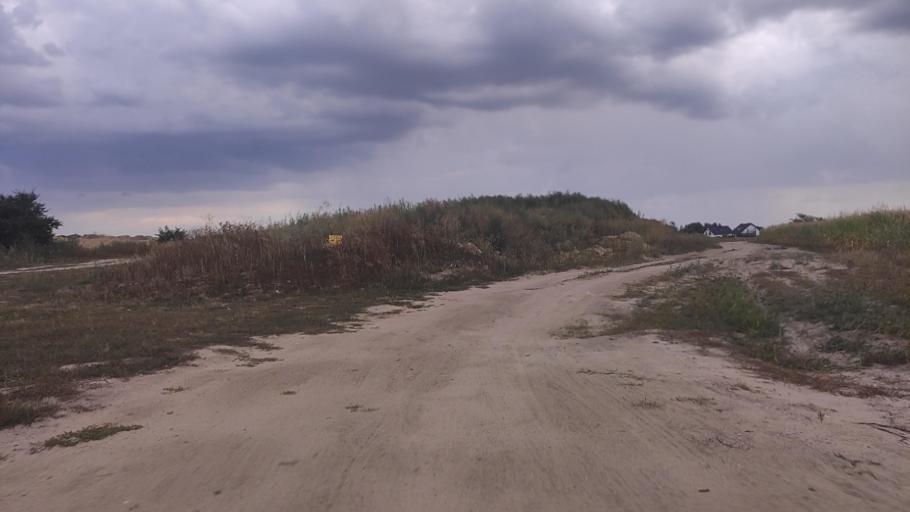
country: PL
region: Greater Poland Voivodeship
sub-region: Powiat poznanski
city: Swarzedz
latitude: 52.3945
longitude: 17.1228
